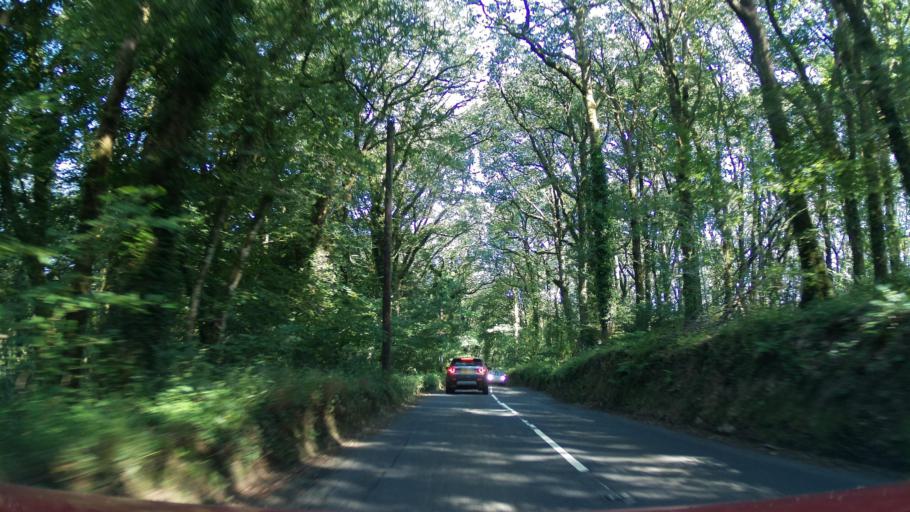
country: GB
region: England
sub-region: Devon
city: Buckfastleigh
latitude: 50.5228
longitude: -3.8081
